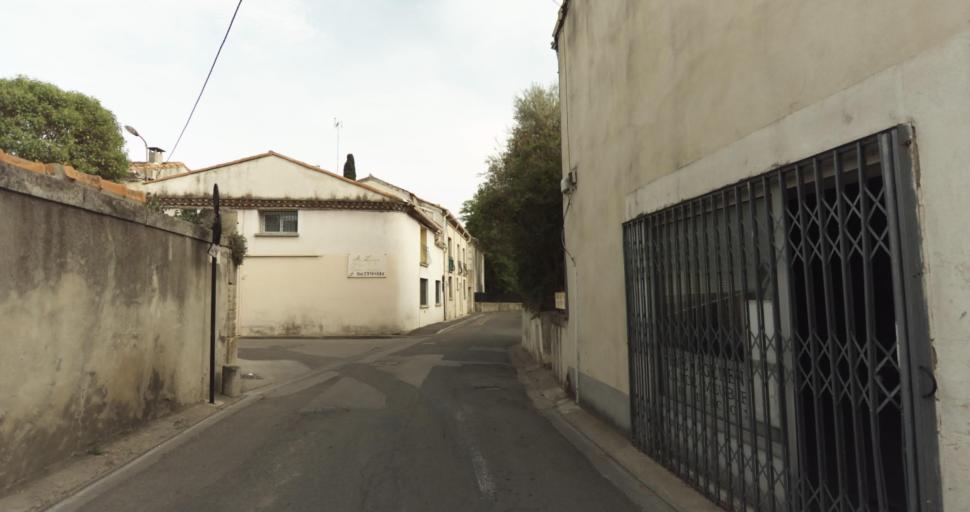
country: FR
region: Languedoc-Roussillon
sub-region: Departement du Gard
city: Nimes
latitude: 43.8157
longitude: 4.3278
